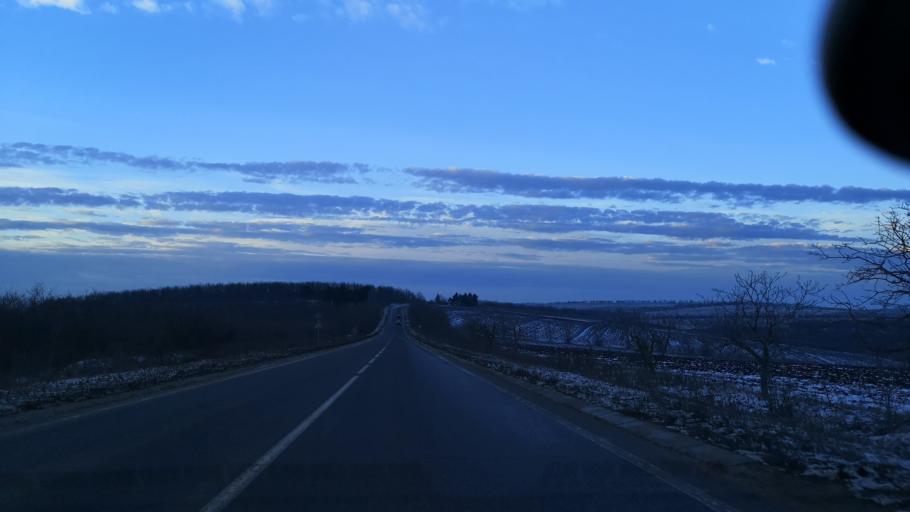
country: MD
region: Orhei
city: Orhei
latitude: 47.5614
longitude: 28.7992
